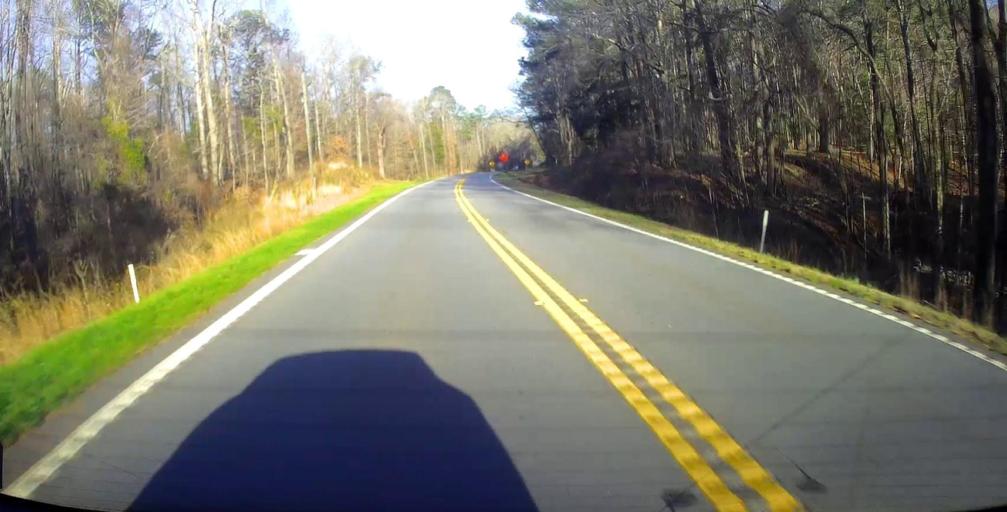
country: US
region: Georgia
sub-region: Harris County
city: Hamilton
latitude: 32.7469
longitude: -85.0261
